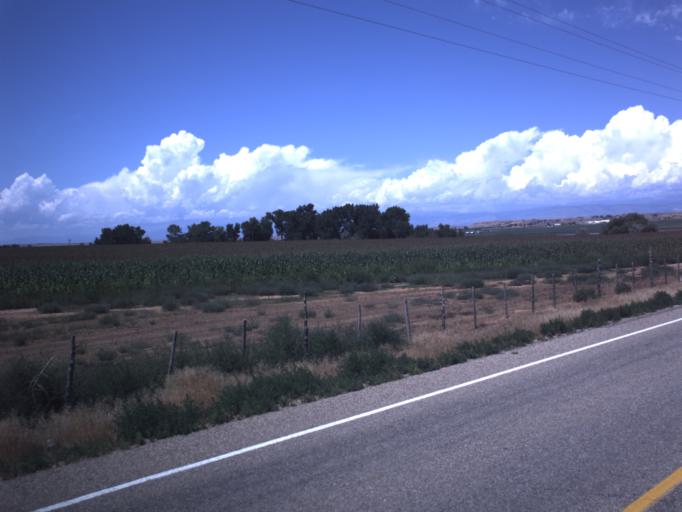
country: US
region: Utah
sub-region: Uintah County
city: Naples
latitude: 40.1823
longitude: -109.6646
